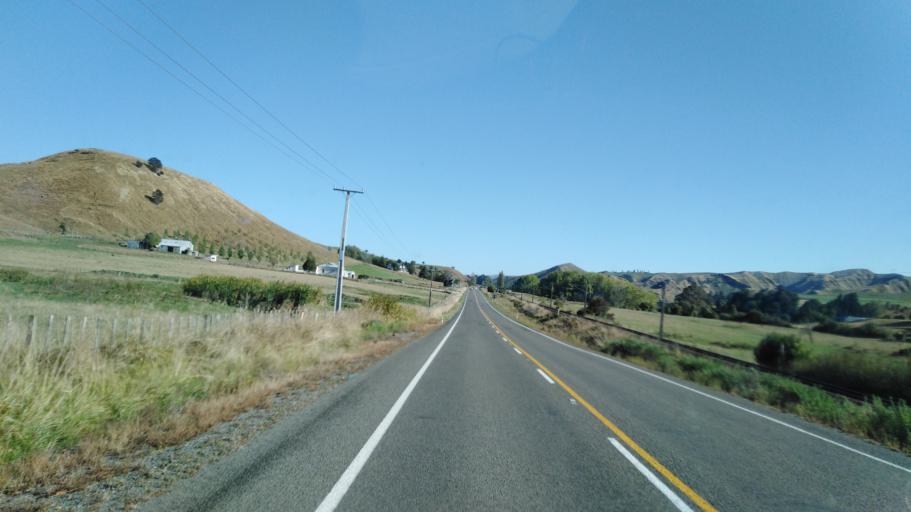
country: NZ
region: Manawatu-Wanganui
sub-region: Ruapehu District
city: Waiouru
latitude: -39.7107
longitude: 175.8367
